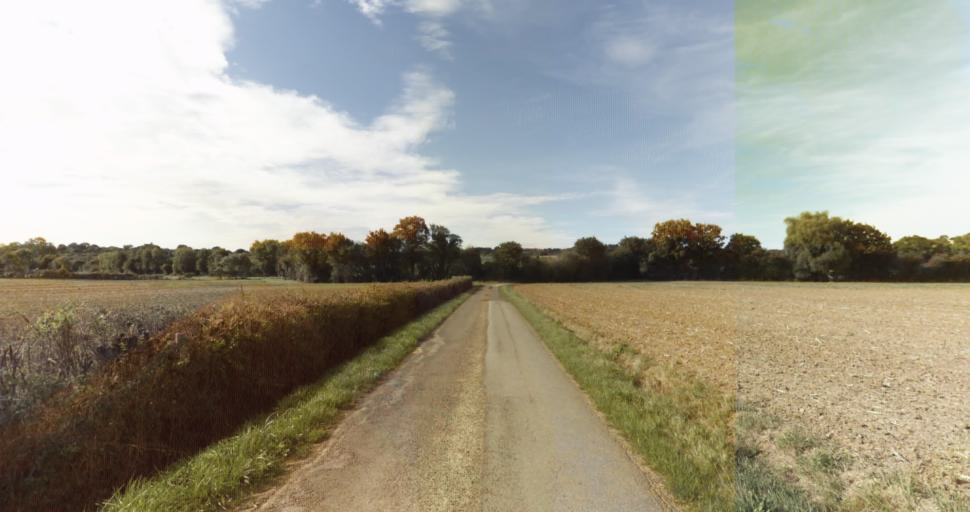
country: FR
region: Lower Normandy
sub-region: Departement de l'Orne
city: Gace
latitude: 48.7188
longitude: 0.2643
